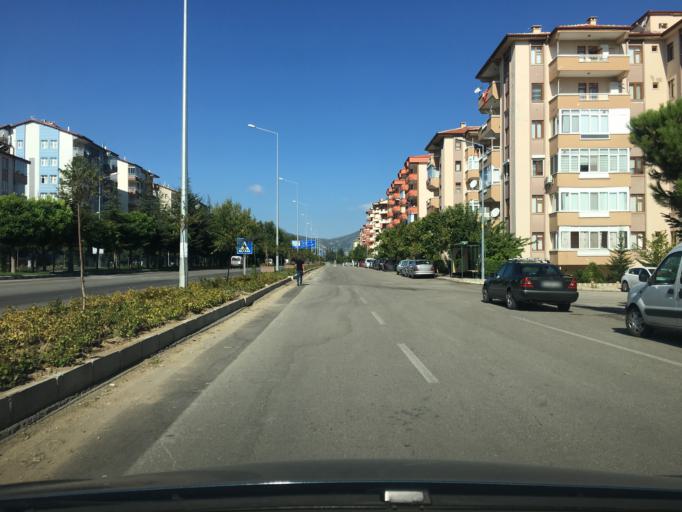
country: TR
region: Isparta
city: Isparta
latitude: 37.7902
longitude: 30.5490
